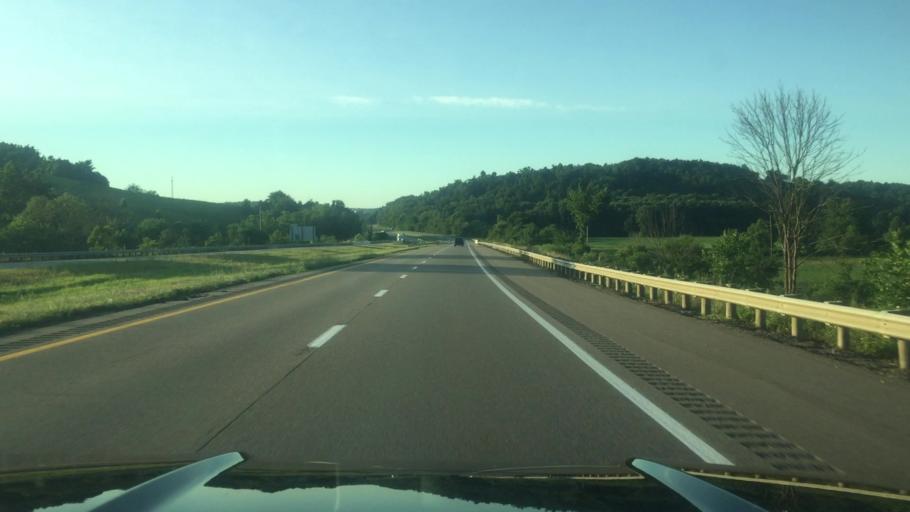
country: US
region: Ohio
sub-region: Tuscarawas County
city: Newcomerstown
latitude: 40.3191
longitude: -81.5696
